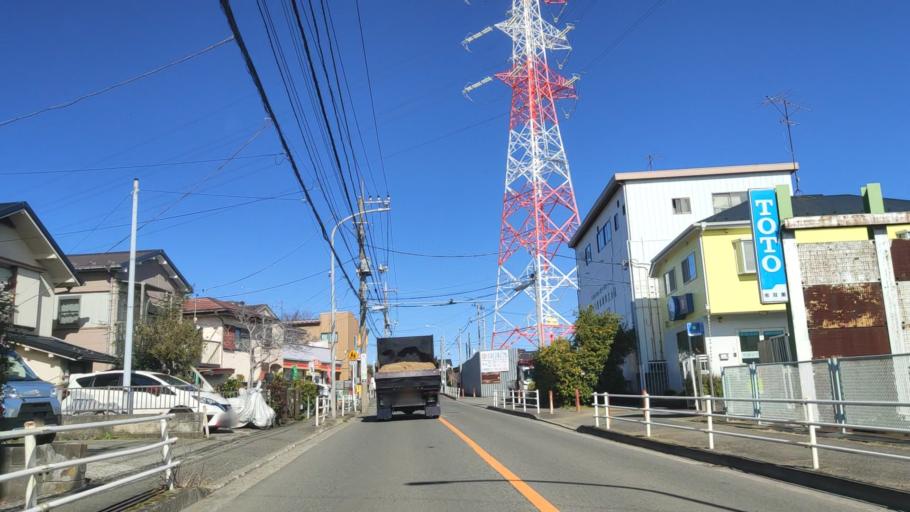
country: JP
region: Kanagawa
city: Minami-rinkan
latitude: 35.4918
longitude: 139.5165
